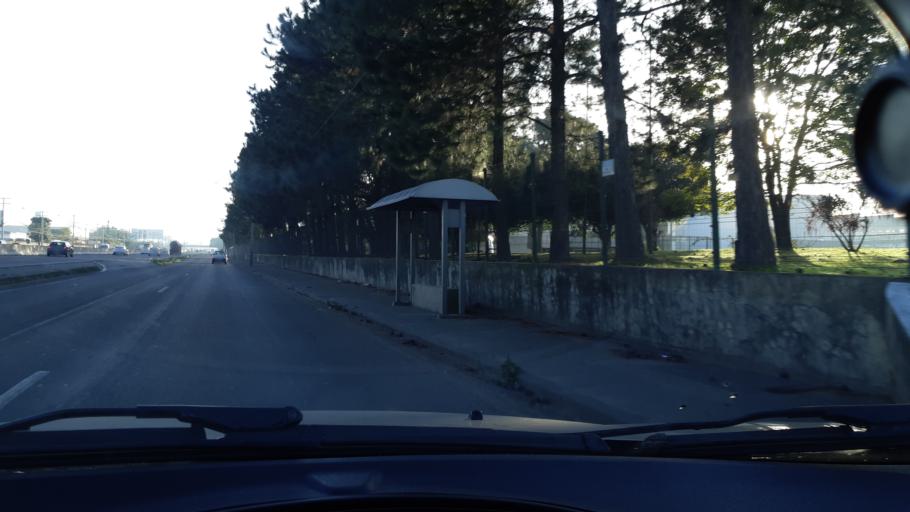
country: BR
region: Rio Grande do Sul
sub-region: Esteio
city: Esteio
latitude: -29.8376
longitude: -51.1754
